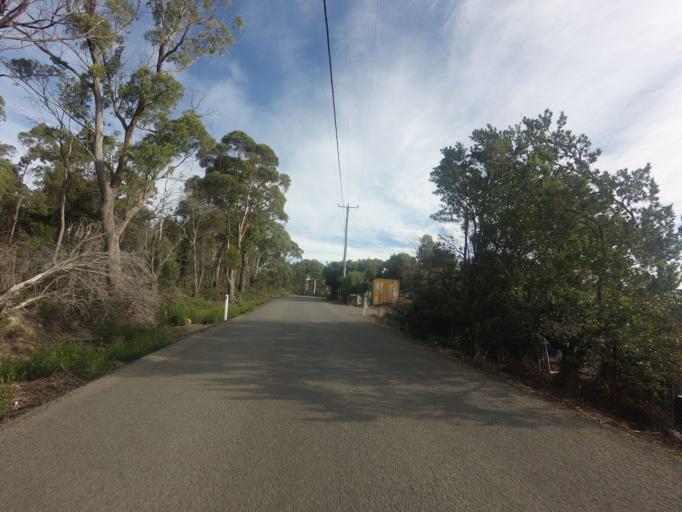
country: AU
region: Tasmania
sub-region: Sorell
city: Sorell
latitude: -42.9616
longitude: 147.8375
